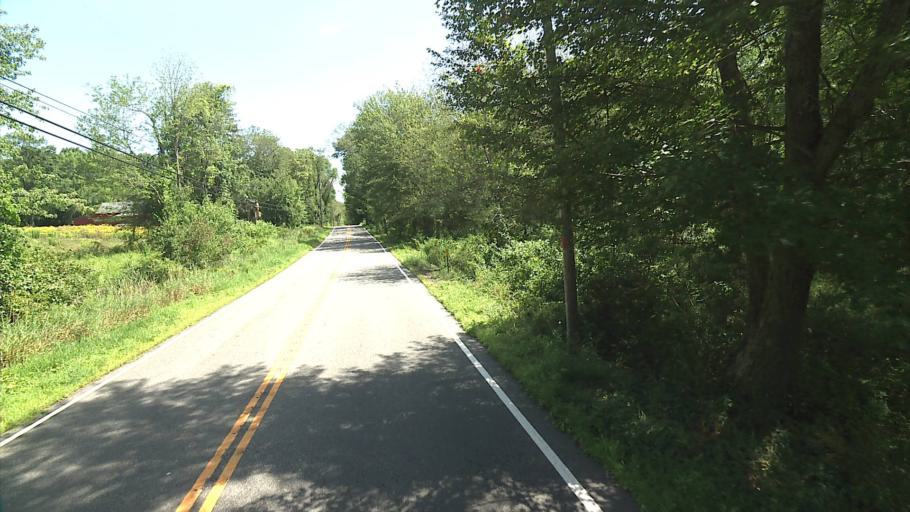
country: US
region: Connecticut
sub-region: Windham County
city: South Woodstock
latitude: 41.8975
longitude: -72.0287
